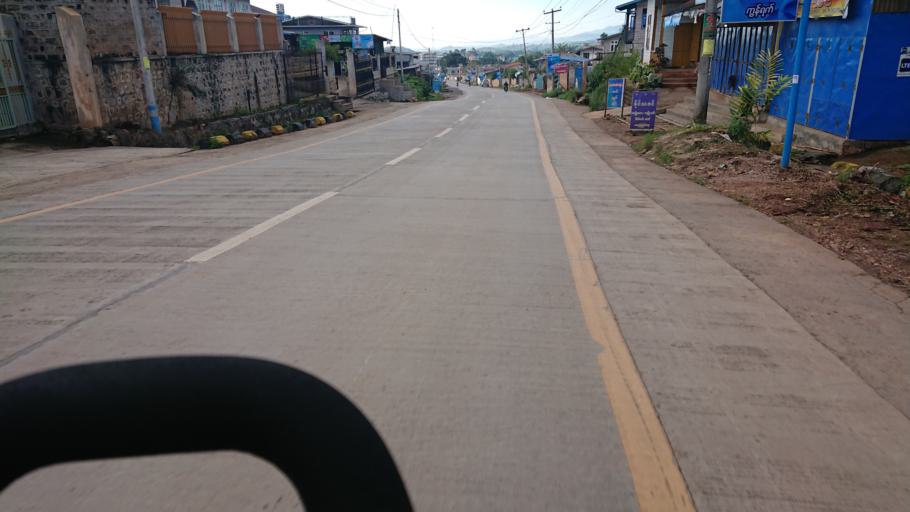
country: MM
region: Shan
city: Taunggyi
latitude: 20.7436
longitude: 97.0507
